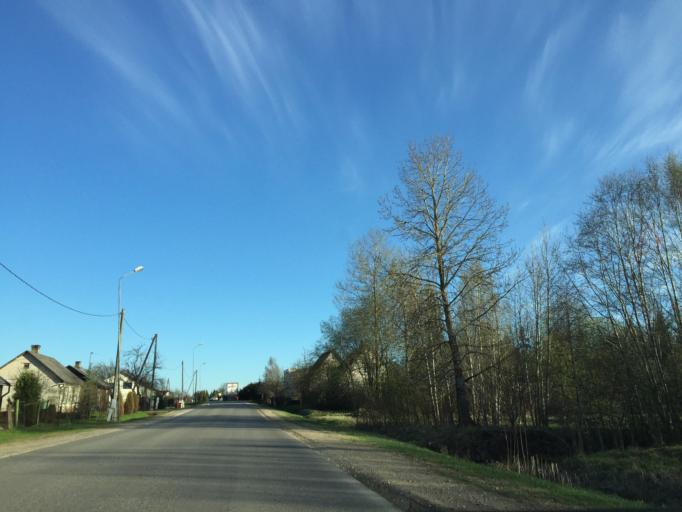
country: LV
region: Valkas Rajons
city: Valka
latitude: 57.7692
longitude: 26.0004
